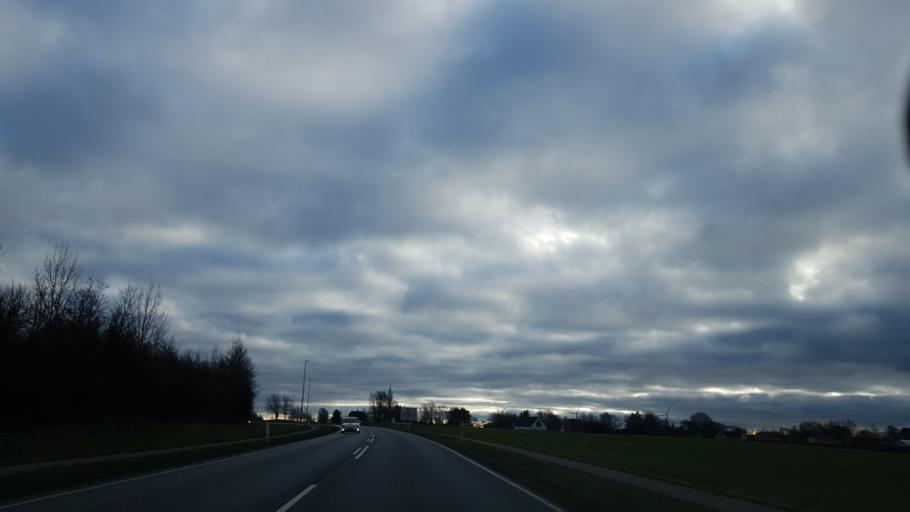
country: DK
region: Zealand
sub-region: Kalundborg Kommune
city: Gorlev
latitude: 55.5377
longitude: 11.2186
